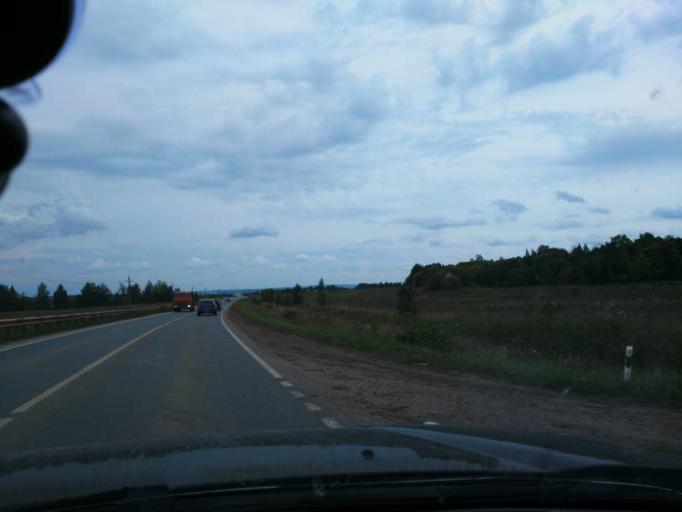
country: RU
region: Perm
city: Chernushka
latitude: 56.5102
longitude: 55.9634
